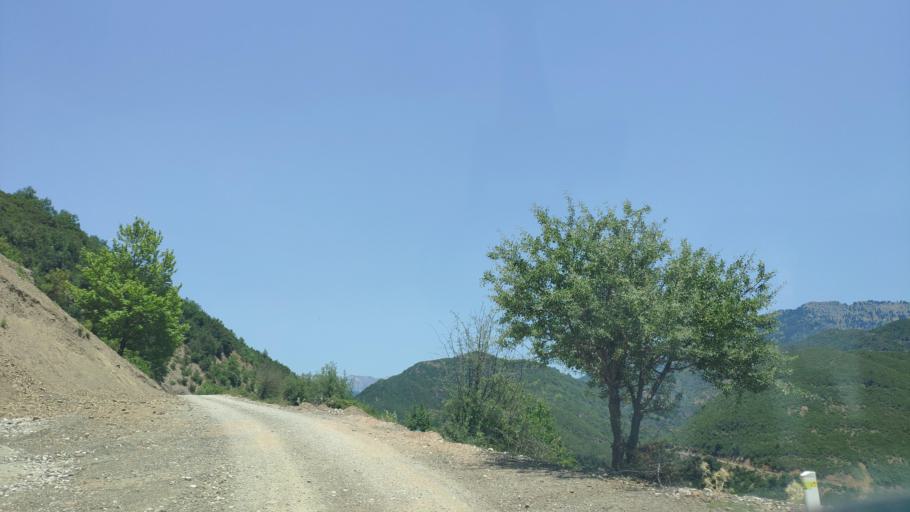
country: GR
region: Thessaly
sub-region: Nomos Kardhitsas
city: Anthiro
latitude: 39.1717
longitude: 21.3708
